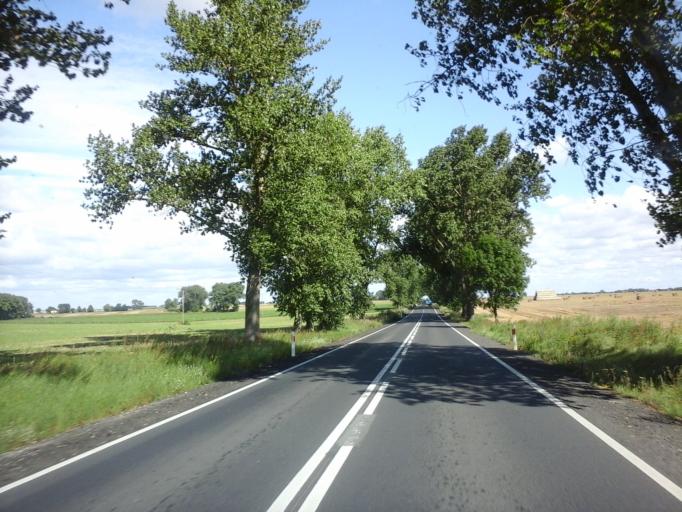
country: PL
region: West Pomeranian Voivodeship
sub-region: Powiat stargardzki
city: Stargard Szczecinski
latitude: 53.2508
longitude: 15.1024
